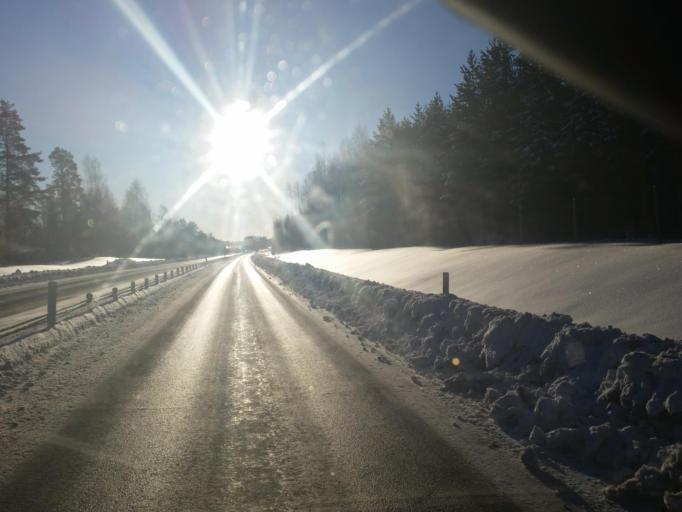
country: SE
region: Norrbotten
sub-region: Pitea Kommun
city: Hortlax
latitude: 65.2909
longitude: 21.4308
